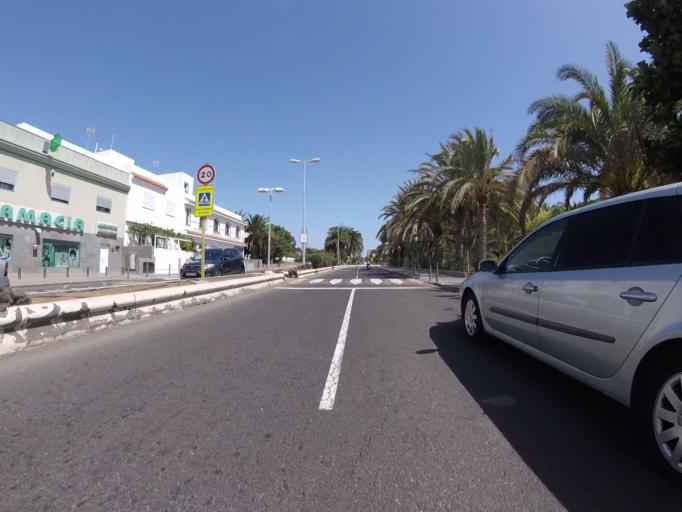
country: ES
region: Canary Islands
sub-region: Provincia de Las Palmas
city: Maspalomas
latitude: 27.7693
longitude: -15.5848
